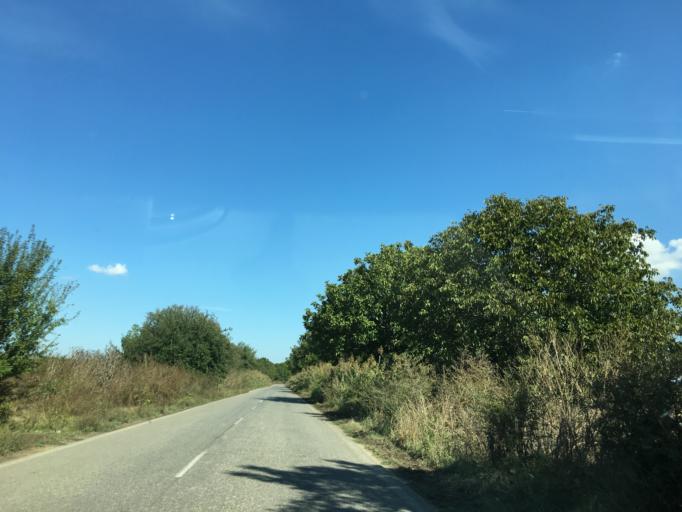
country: RO
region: Olt
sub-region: Comuna Orlea
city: Orlea
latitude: 43.6143
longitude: 24.3686
